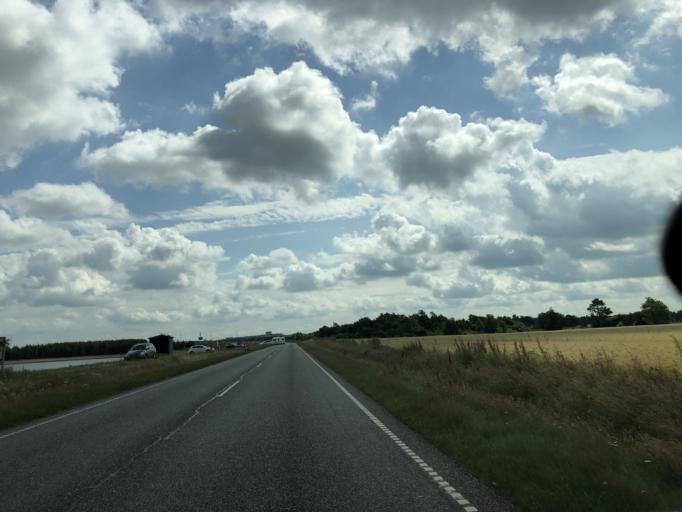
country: DK
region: Central Jutland
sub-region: Herning Kommune
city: Lind
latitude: 56.0134
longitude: 9.0147
